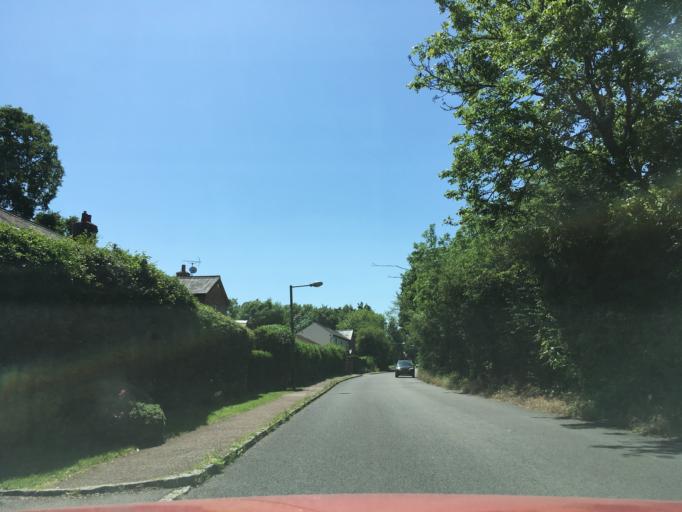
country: GB
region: England
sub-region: Milton Keynes
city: Simpson
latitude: 52.0337
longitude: -0.7236
